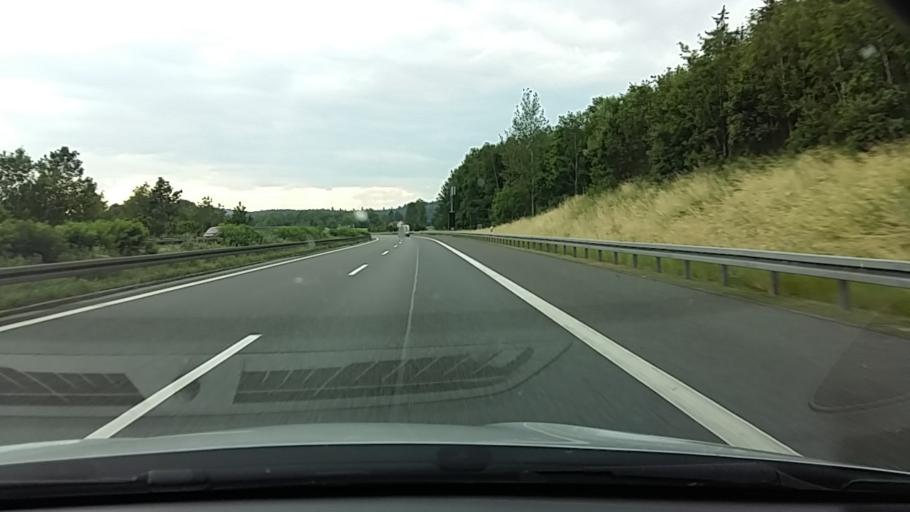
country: DE
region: Bavaria
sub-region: Upper Palatinate
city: Waidhaus
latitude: 49.6331
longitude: 12.4624
